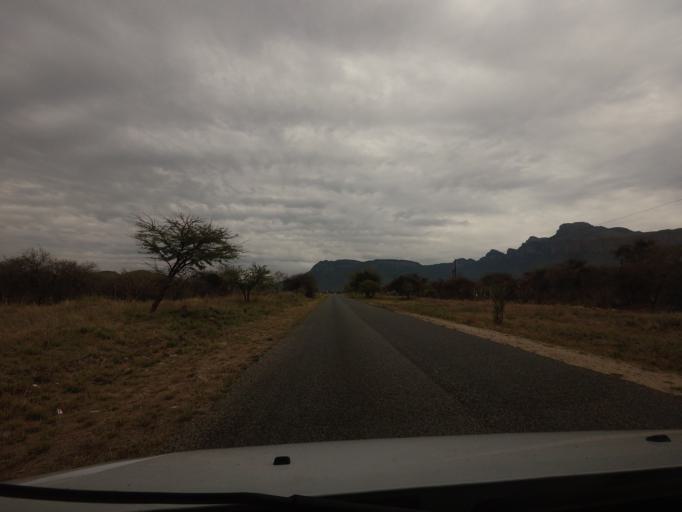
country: ZA
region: Limpopo
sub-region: Mopani District Municipality
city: Hoedspruit
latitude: -24.4926
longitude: 30.8913
